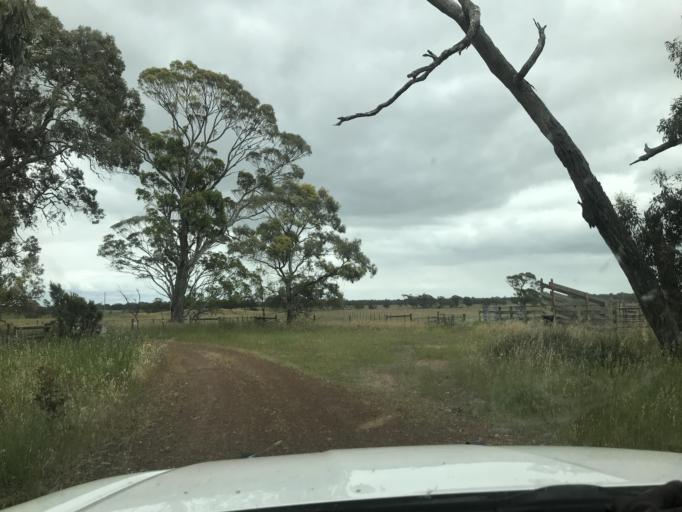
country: AU
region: South Australia
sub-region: Wattle Range
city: Penola
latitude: -37.0978
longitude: 141.2682
